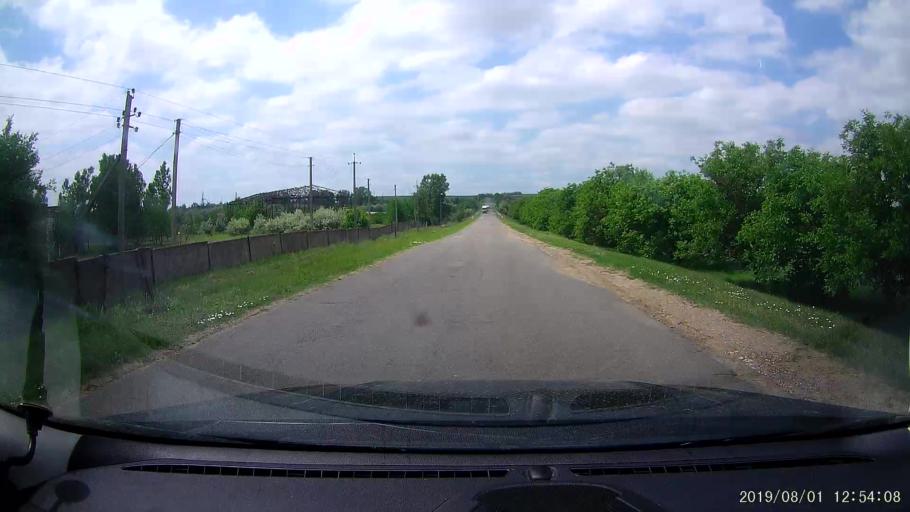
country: UA
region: Odessa
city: Vynohradivka
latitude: 45.6965
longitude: 28.4923
